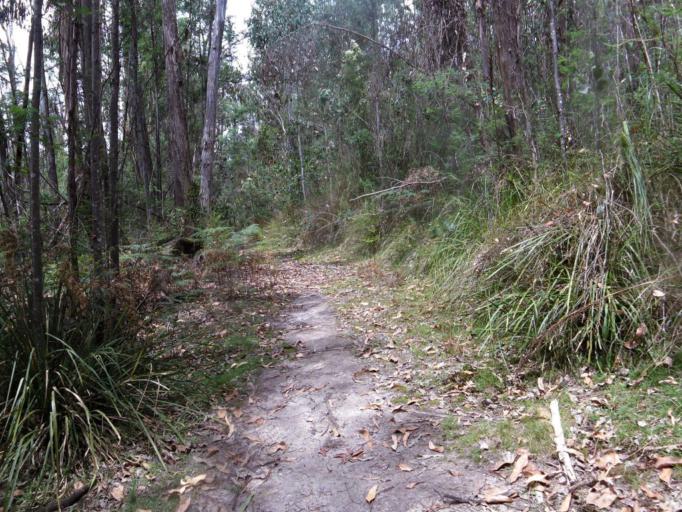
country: AU
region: Victoria
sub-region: Yarra Ranges
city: Healesville
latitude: -37.4344
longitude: 145.5738
